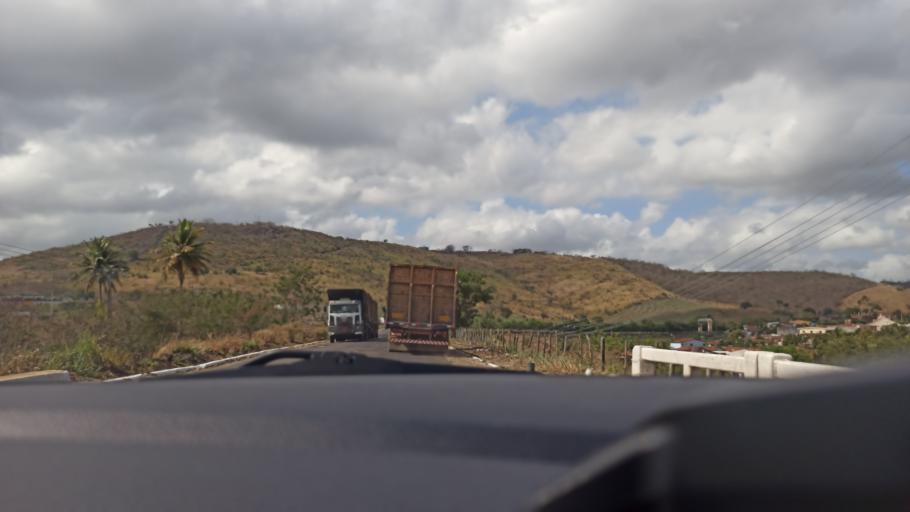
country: BR
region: Pernambuco
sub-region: Timbauba
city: Timbauba
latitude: -7.5174
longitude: -35.3045
